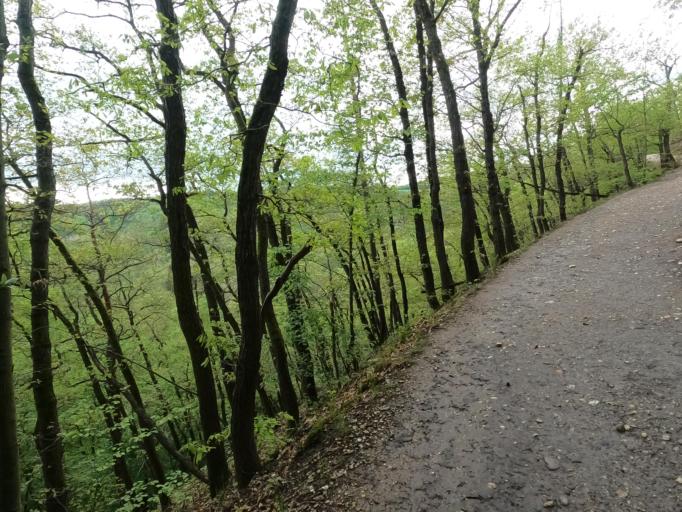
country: DE
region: Rheinland-Pfalz
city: Wierschem
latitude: 50.2114
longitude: 7.3364
